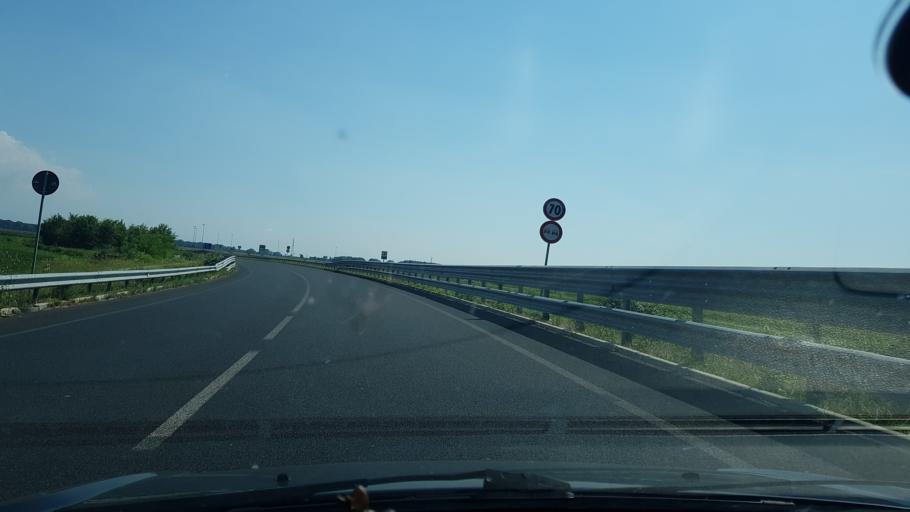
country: IT
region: Friuli Venezia Giulia
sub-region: Provincia di Gorizia
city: Staranzano
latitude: 45.7970
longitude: 13.4886
